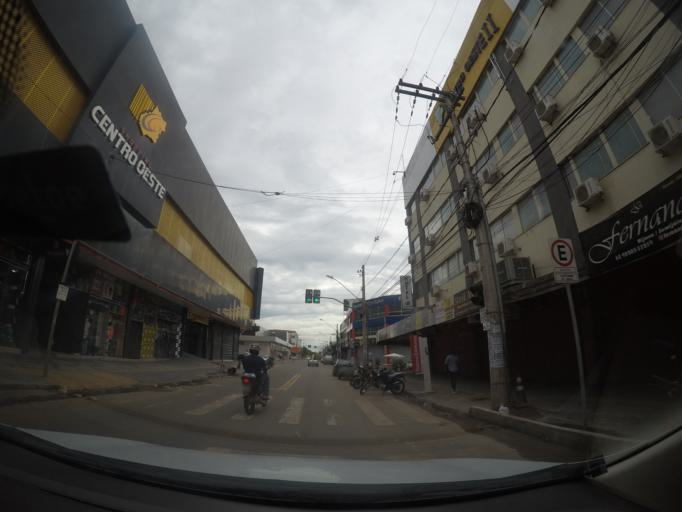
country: BR
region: Goias
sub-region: Goiania
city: Goiania
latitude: -16.6591
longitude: -49.2560
